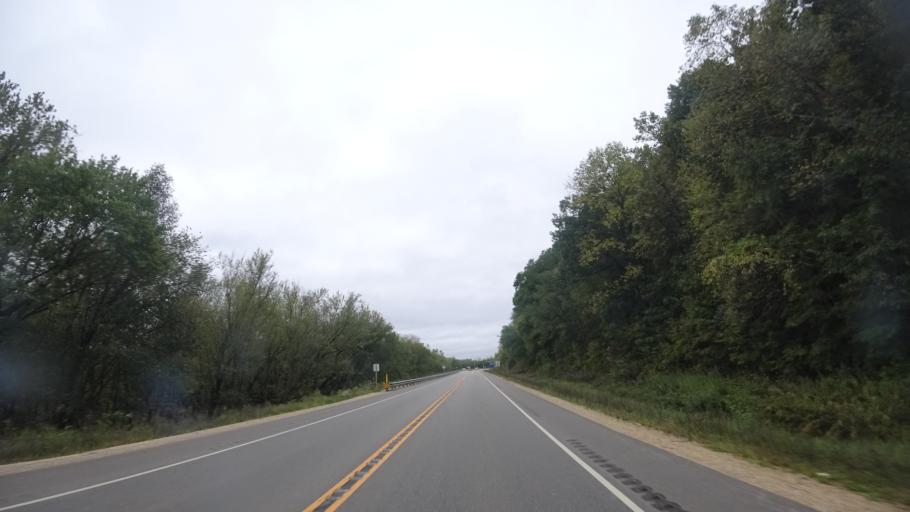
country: US
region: Wisconsin
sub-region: Grant County
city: Boscobel
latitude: 43.1558
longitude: -90.7129
